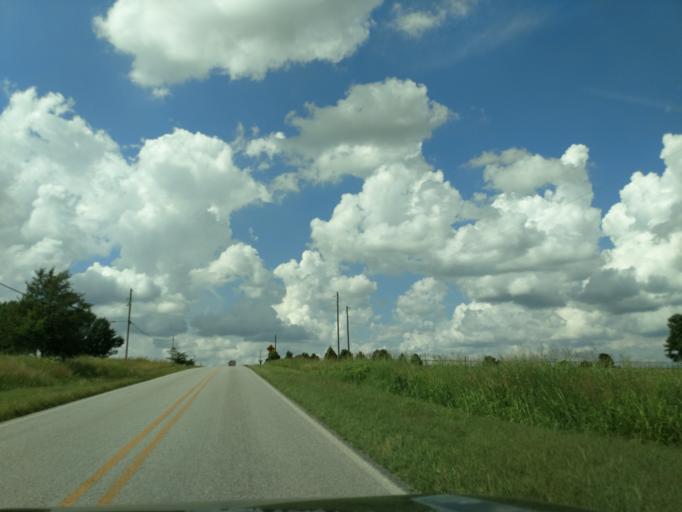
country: US
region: Arkansas
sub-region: Carroll County
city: Berryville
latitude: 36.4342
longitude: -93.5563
